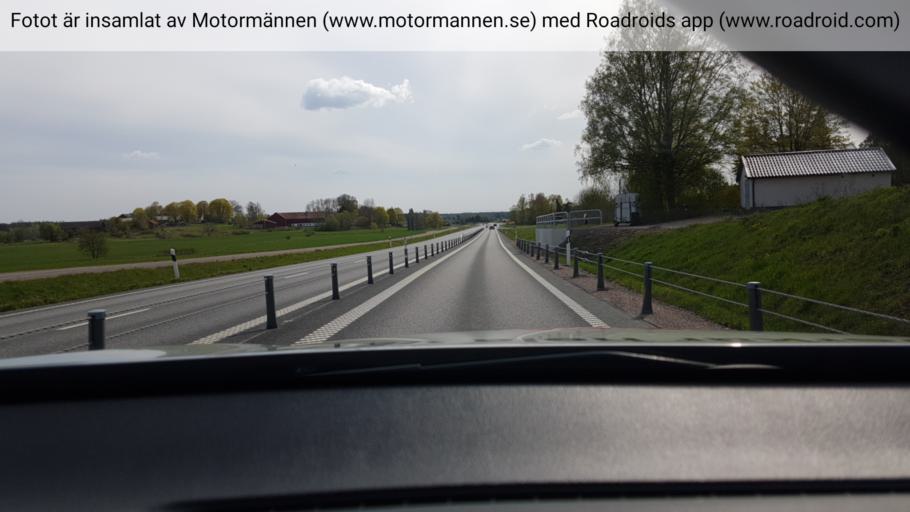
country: SE
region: Uppsala
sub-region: Osthammars Kommun
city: Gimo
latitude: 60.0967
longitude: 18.1243
